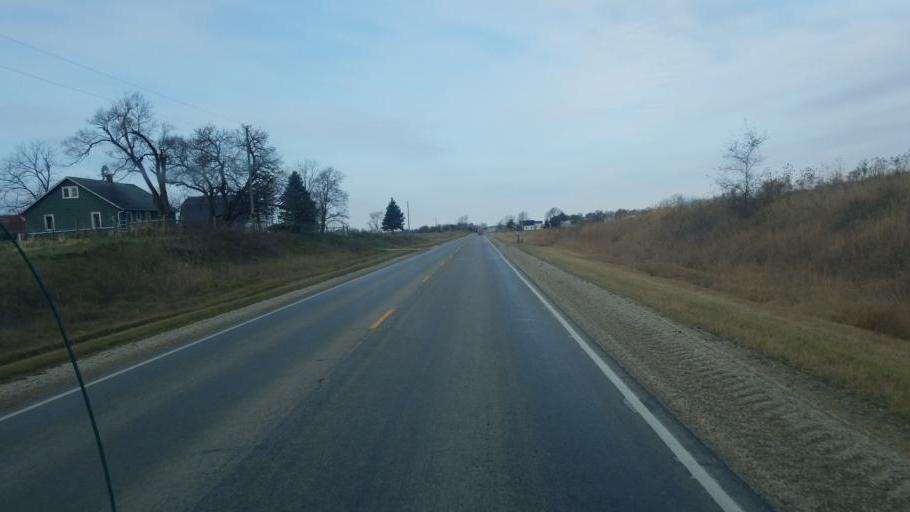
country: US
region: Indiana
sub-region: Adams County
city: Geneva
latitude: 40.5416
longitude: -84.9282
